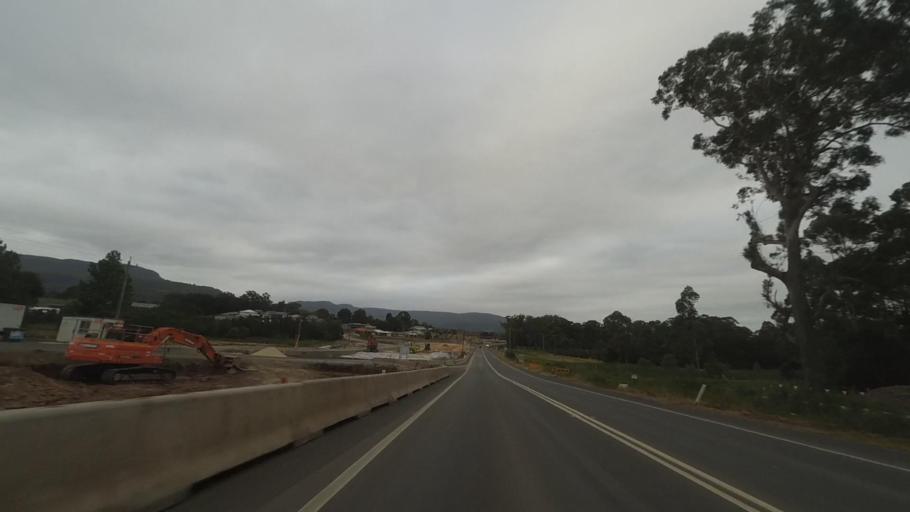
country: AU
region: New South Wales
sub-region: Shoalhaven Shire
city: Berry
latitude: -34.7777
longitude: 150.6827
